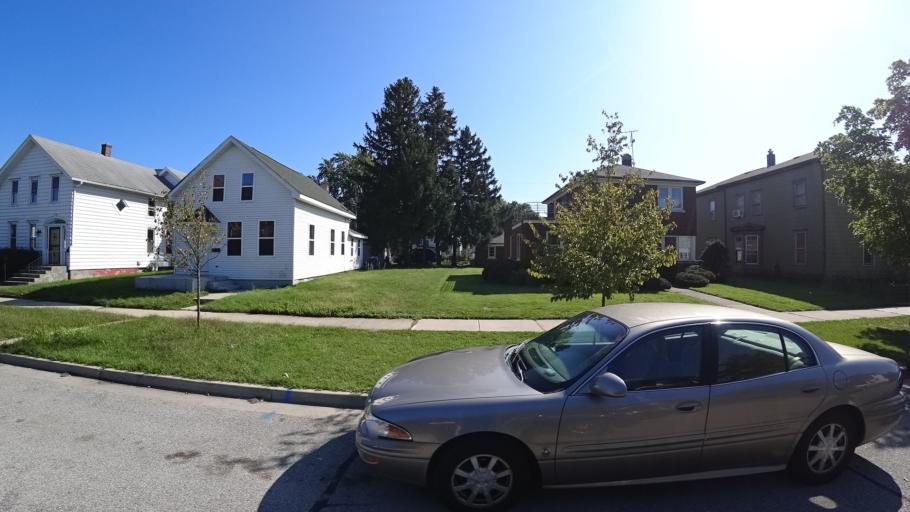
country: US
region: Indiana
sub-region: LaPorte County
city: Michigan City
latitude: 41.7127
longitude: -86.8972
